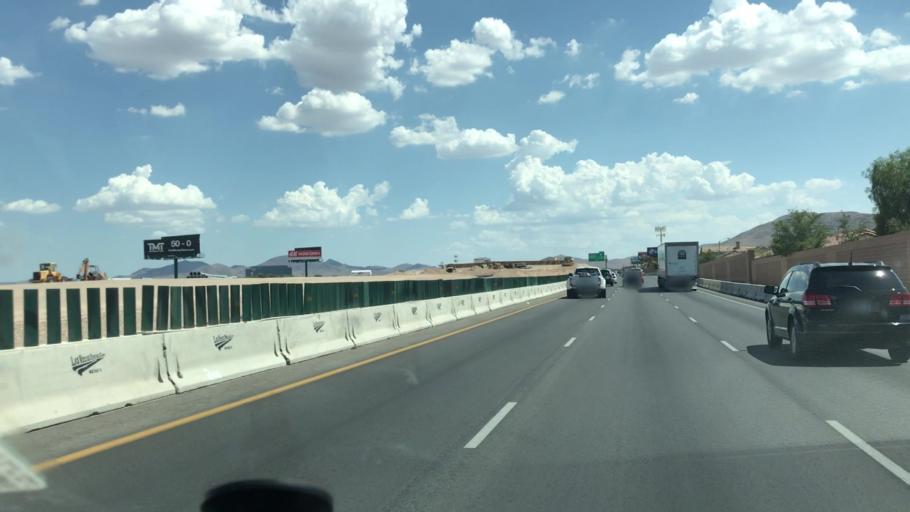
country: US
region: Nevada
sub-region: Clark County
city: Enterprise
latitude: 35.9881
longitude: -115.1814
